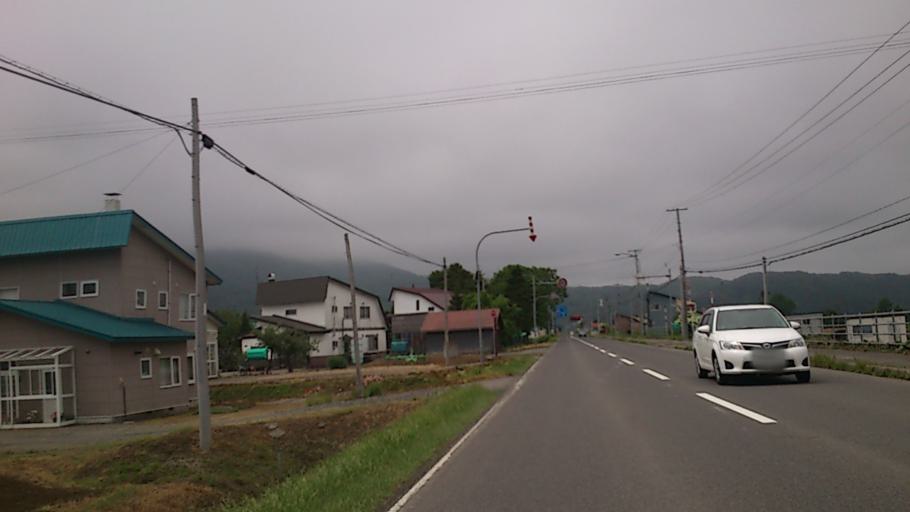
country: JP
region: Hokkaido
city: Iwanai
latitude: 42.8005
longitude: 140.4955
